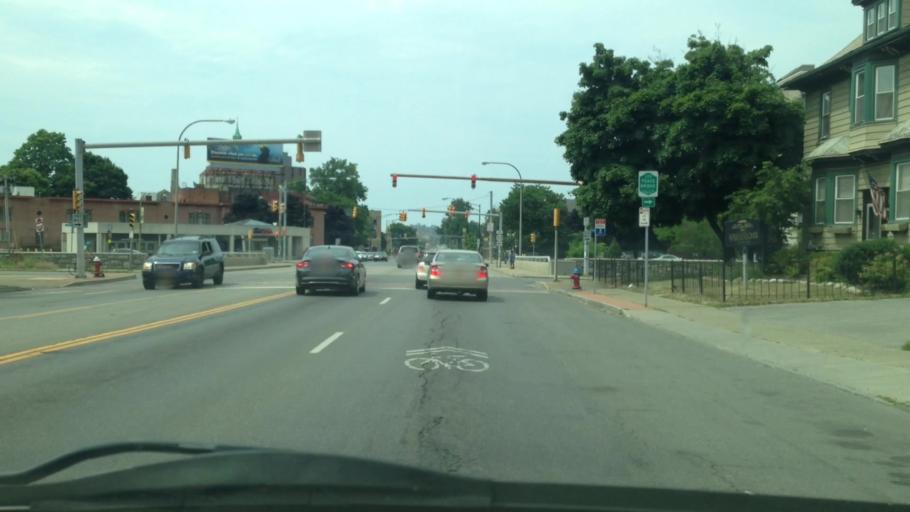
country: US
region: New York
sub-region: Erie County
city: Kenmore
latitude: 42.9285
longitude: -78.8507
